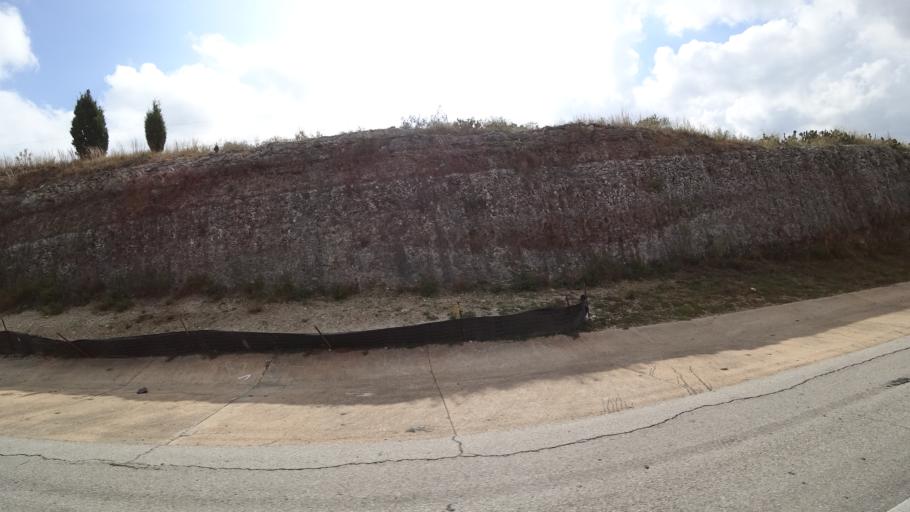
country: US
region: Texas
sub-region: Travis County
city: Hudson Bend
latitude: 30.3939
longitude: -97.8709
